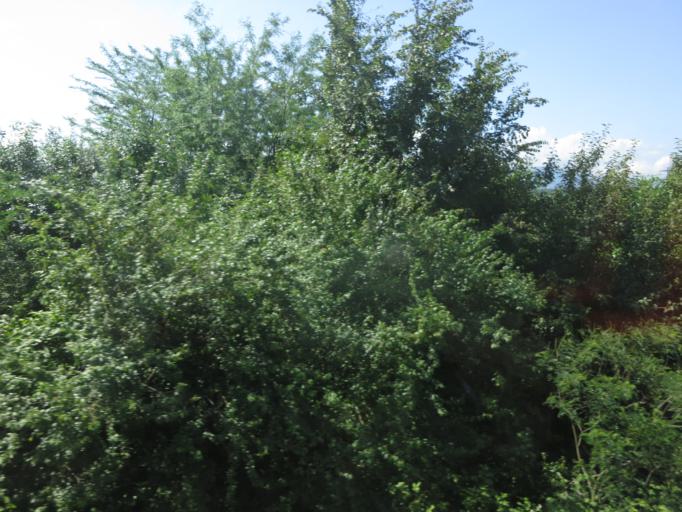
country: GE
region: Imereti
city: Zestap'oni
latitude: 42.1584
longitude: 42.9141
